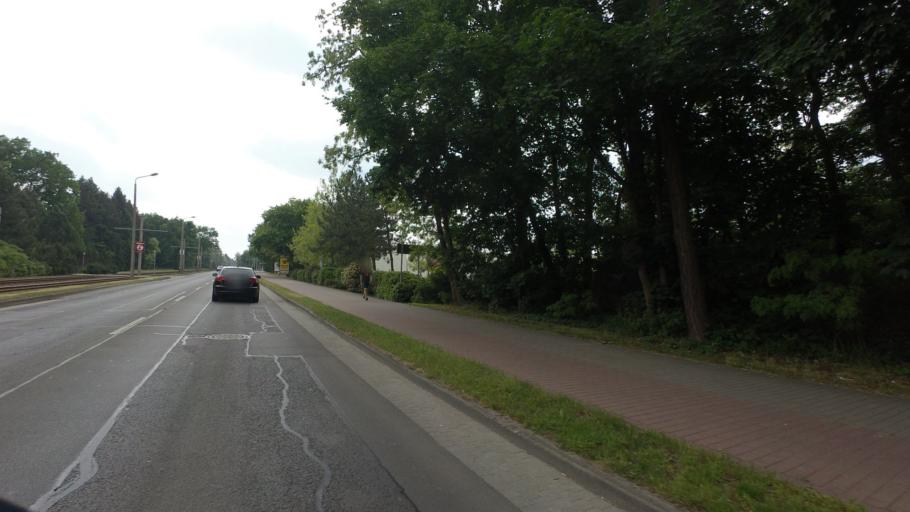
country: DE
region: Brandenburg
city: Cottbus
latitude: 51.7366
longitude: 14.3364
